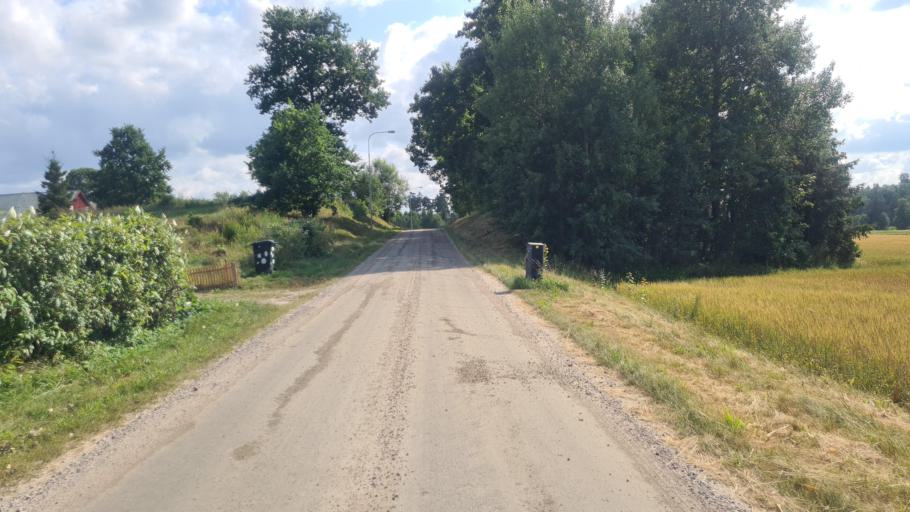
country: SE
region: Kronoberg
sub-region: Ljungby Kommun
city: Ljungby
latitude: 56.7339
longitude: 13.8715
